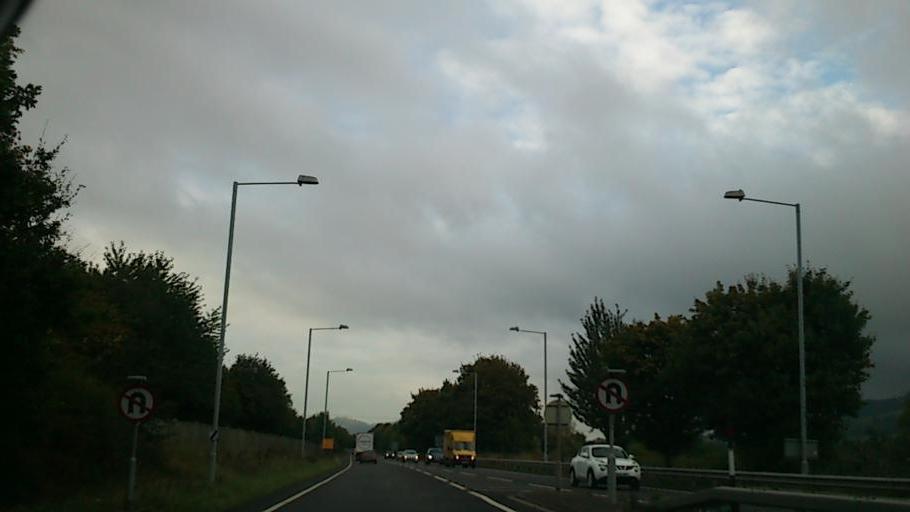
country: GB
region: Wales
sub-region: Sir Powys
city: Welshpool
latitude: 52.6652
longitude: -3.1298
